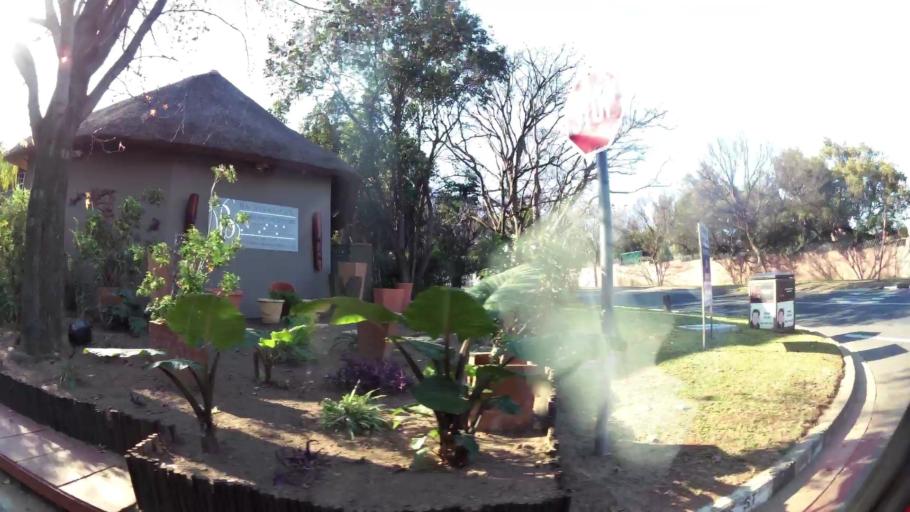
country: ZA
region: Gauteng
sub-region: City of Johannesburg Metropolitan Municipality
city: Roodepoort
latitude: -26.0994
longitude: 27.9518
